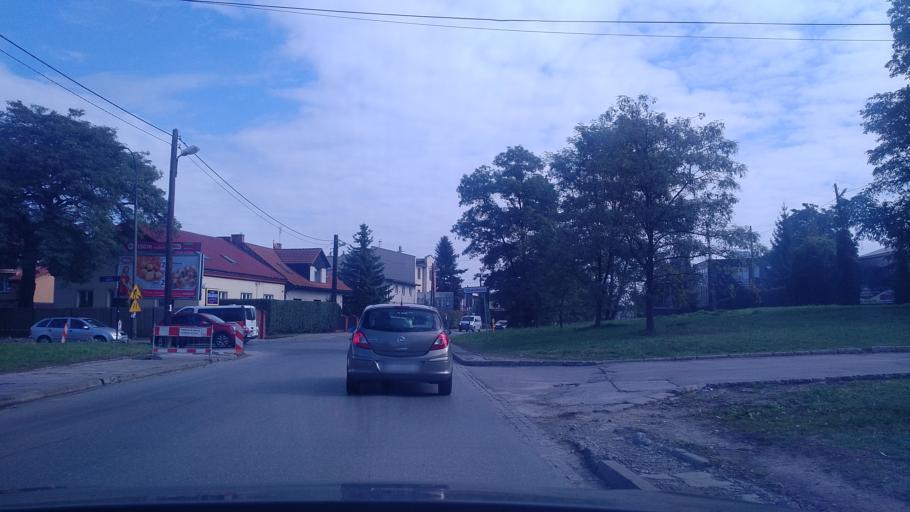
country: PL
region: Lesser Poland Voivodeship
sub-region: Krakow
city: Krakow
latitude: 50.0834
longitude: 19.9077
